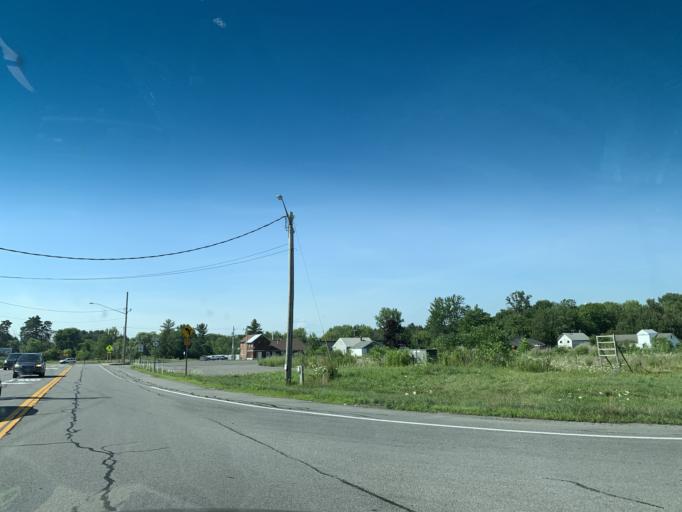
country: US
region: New York
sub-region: Oneida County
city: Sherrill
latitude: 43.1301
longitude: -75.5783
